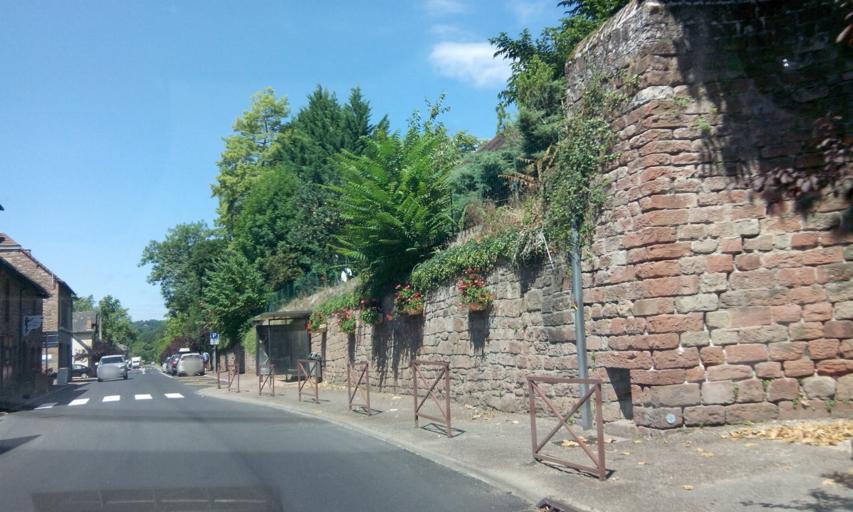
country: FR
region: Limousin
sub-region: Departement de la Correze
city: Meyssac
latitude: 45.0560
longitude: 1.6725
